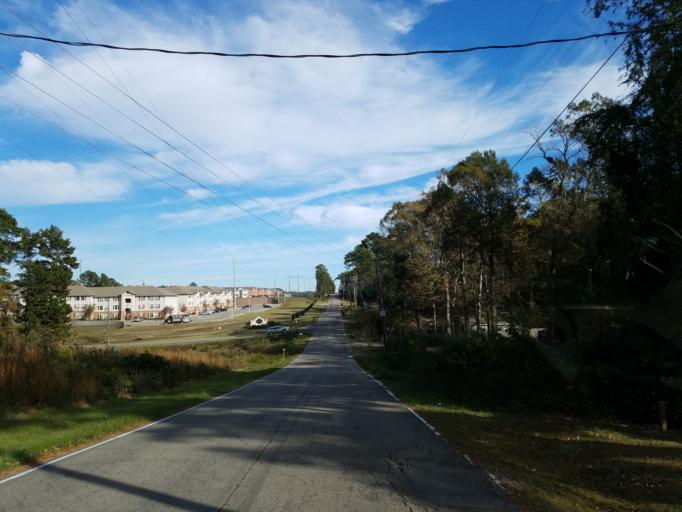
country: US
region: Mississippi
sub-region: Lamar County
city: Arnold Line
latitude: 31.3466
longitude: -89.3430
